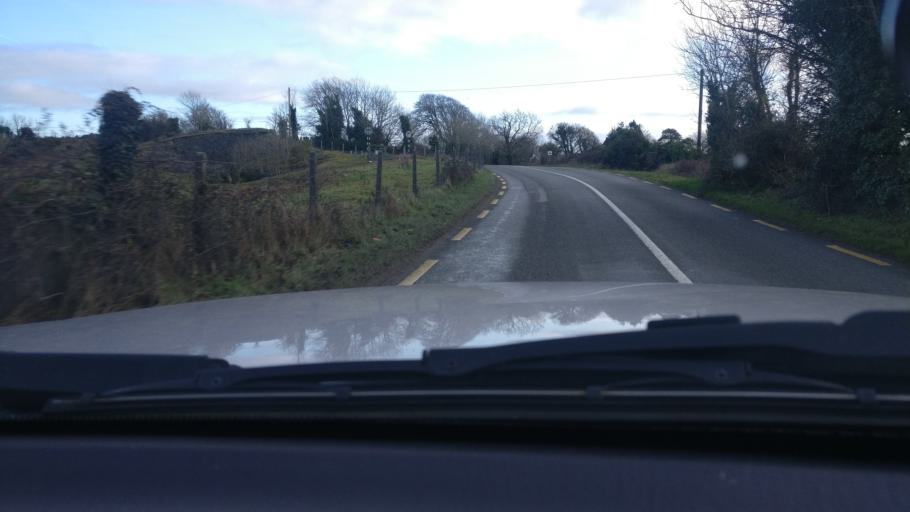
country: IE
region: Connaught
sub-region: County Galway
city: Ballinasloe
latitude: 53.2940
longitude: -8.2420
